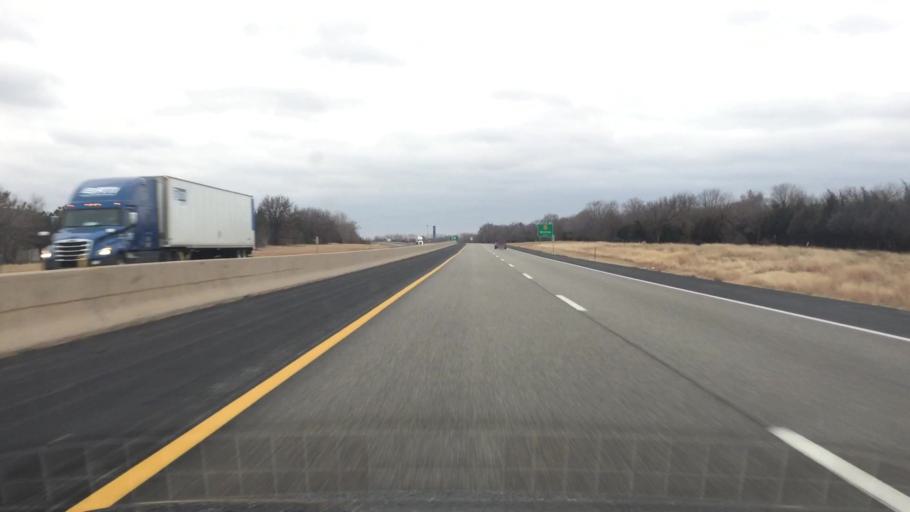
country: US
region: Kansas
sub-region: Butler County
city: Andover
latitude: 37.6991
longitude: -97.1595
